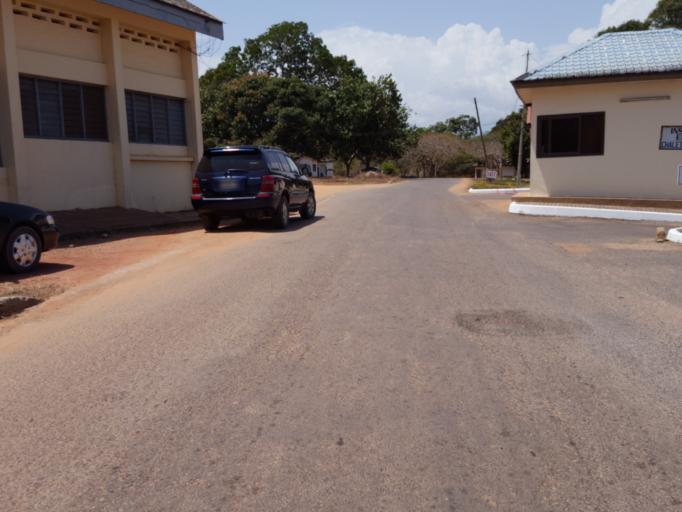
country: GH
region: Central
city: Cape Coast
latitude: 5.1209
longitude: -1.2902
